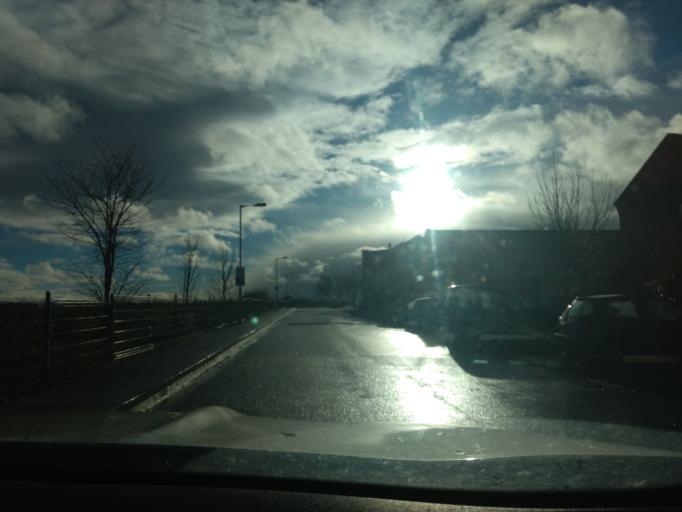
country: IE
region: Leinster
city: Kinsealy-Drinan
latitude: 53.4512
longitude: -6.1979
